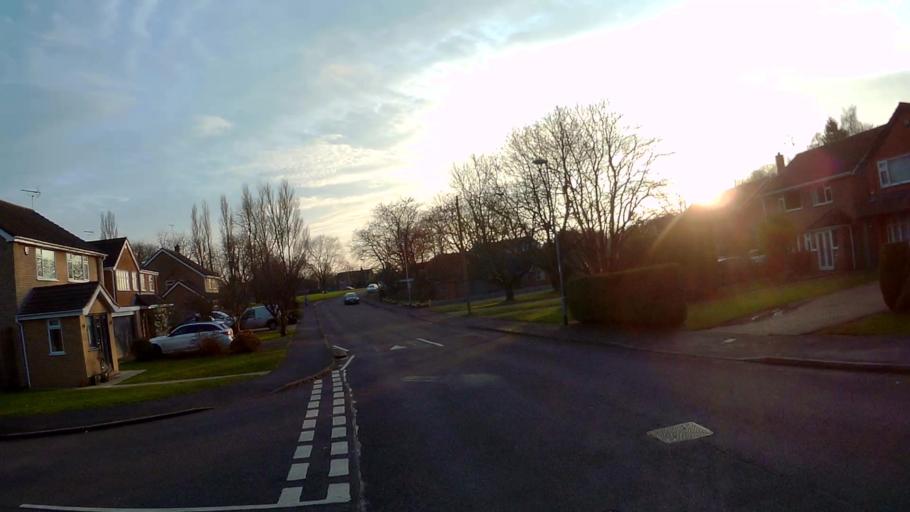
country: GB
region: England
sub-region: Lincolnshire
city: Bourne
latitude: 52.7717
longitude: -0.3921
